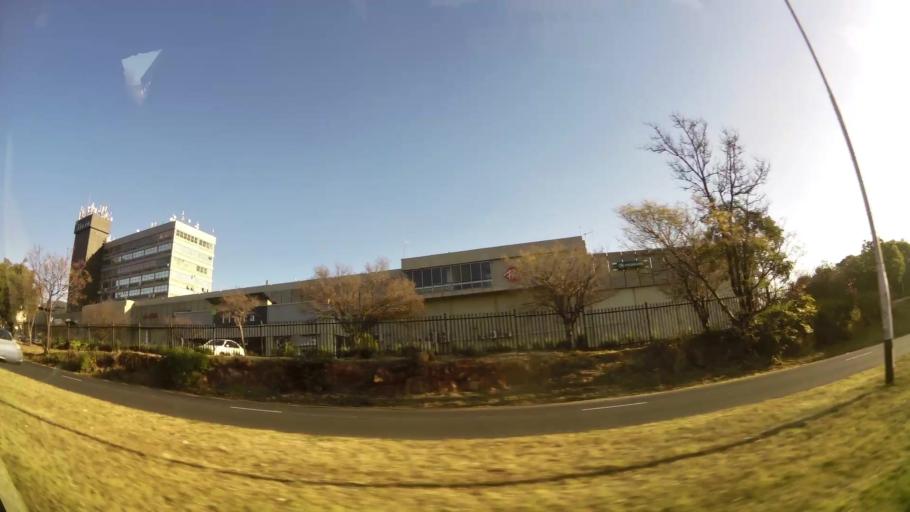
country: ZA
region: Gauteng
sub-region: City of Johannesburg Metropolitan Municipality
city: Roodepoort
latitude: -26.1662
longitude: 27.9274
